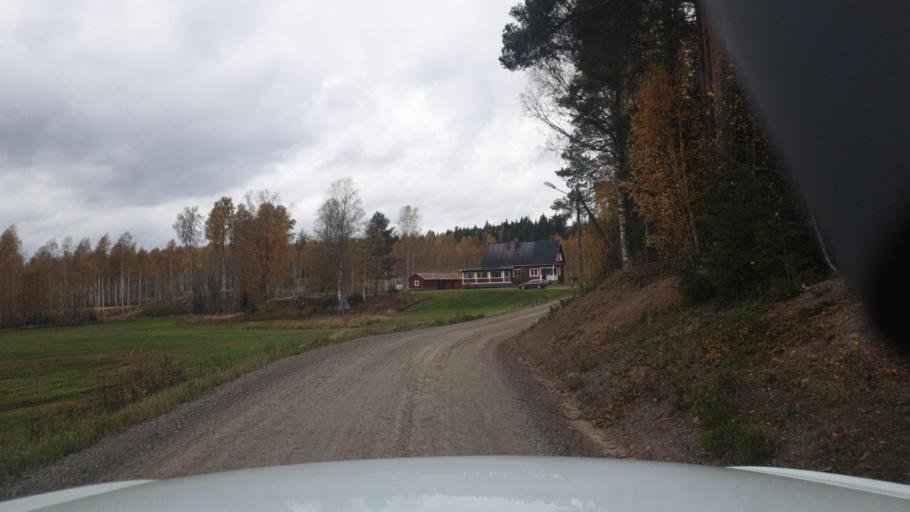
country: SE
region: Vaermland
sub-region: Arvika Kommun
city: Arvika
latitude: 59.9390
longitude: 12.6625
